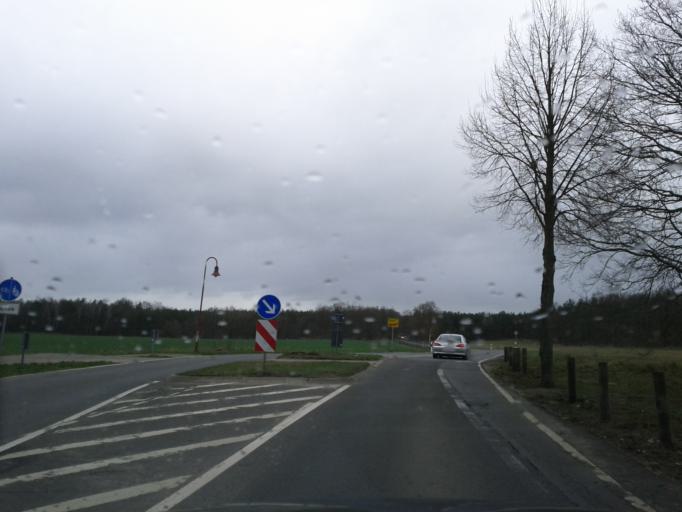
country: DE
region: Brandenburg
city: Woltersdorf
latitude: 52.4662
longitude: 13.7471
